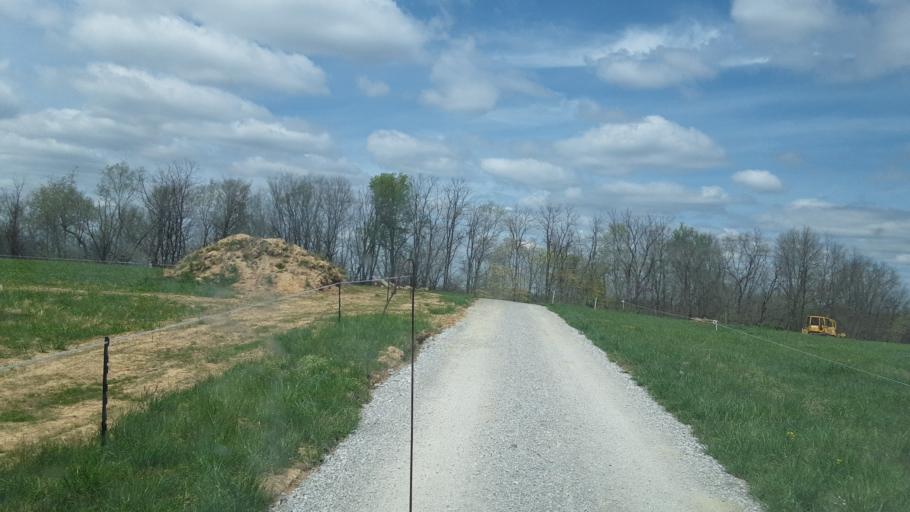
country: US
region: Kentucky
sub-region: Gallatin County
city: Warsaw
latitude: 38.6808
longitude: -84.8066
